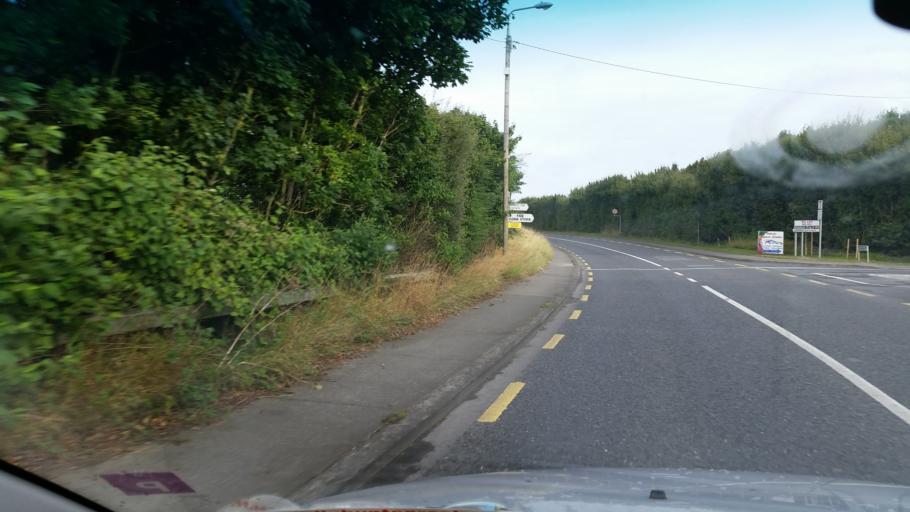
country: IE
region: Leinster
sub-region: Dublin City
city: Finglas
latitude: 53.4077
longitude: -6.3008
